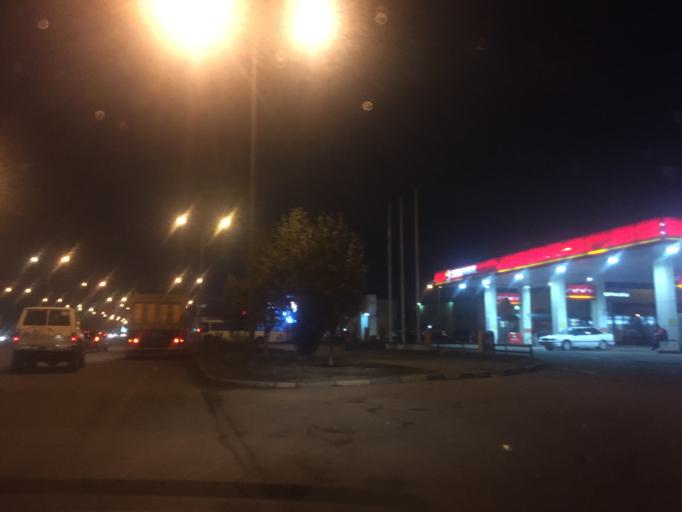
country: KZ
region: Astana Qalasy
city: Astana
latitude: 51.1786
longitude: 71.3847
